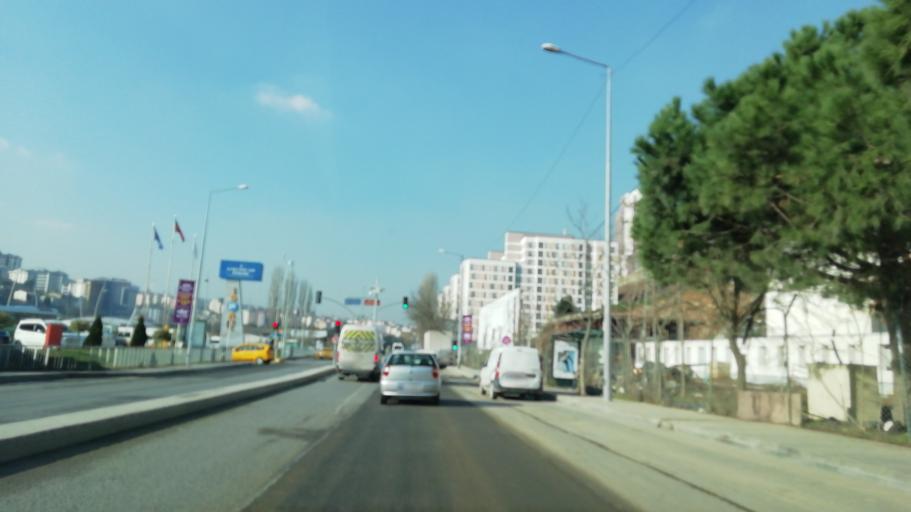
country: TR
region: Istanbul
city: Sisli
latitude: 41.0883
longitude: 28.9451
